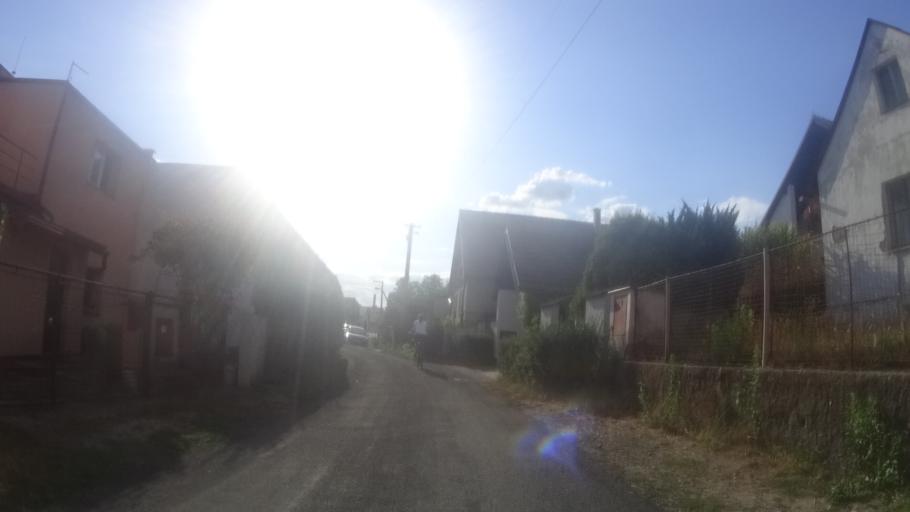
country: CZ
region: Kralovehradecky
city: Trebechovice pod Orebem
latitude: 50.1994
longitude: 15.9980
